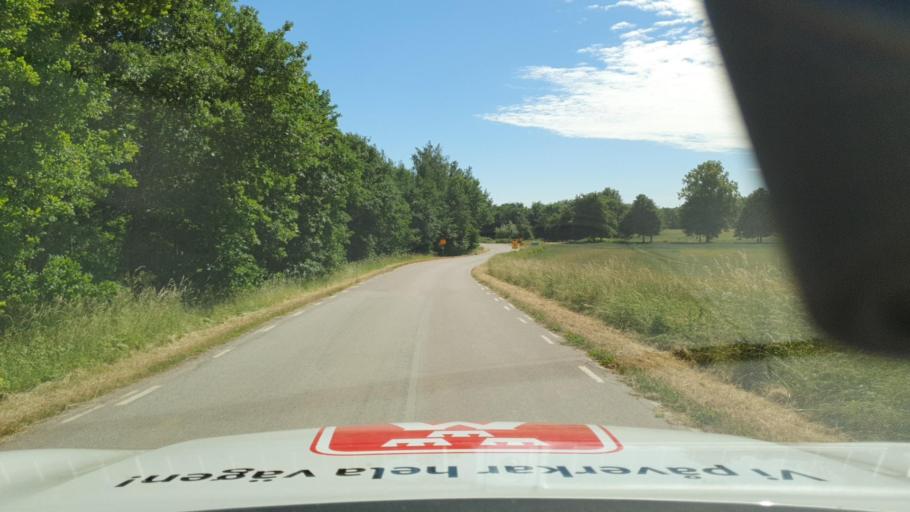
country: SE
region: Skane
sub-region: Eslovs Kommun
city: Eslov
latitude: 55.7842
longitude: 13.2524
